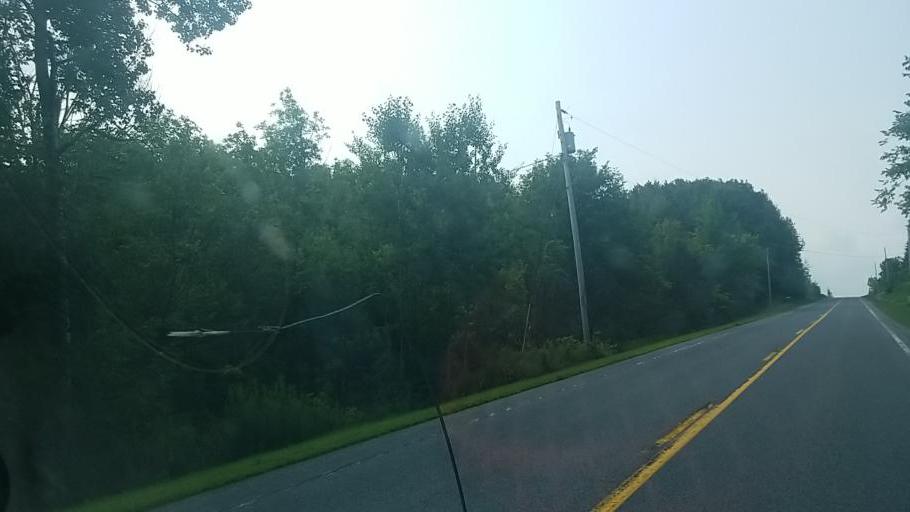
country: US
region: New York
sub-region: Fulton County
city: Johnstown
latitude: 43.0111
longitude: -74.4051
